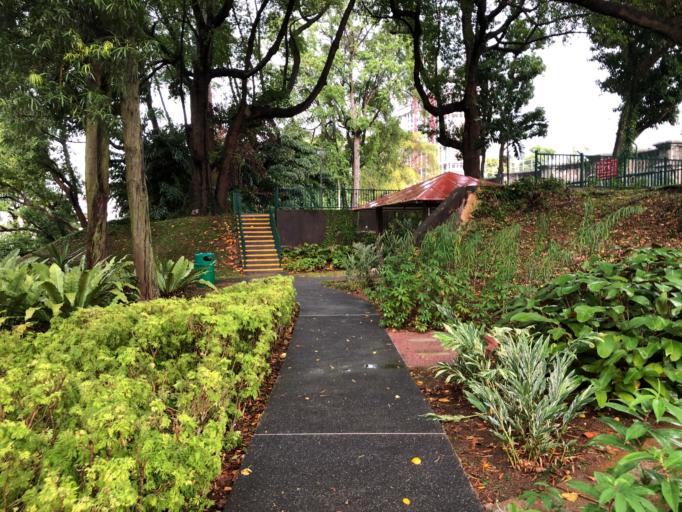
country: SG
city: Singapore
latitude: 1.2847
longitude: 103.8390
